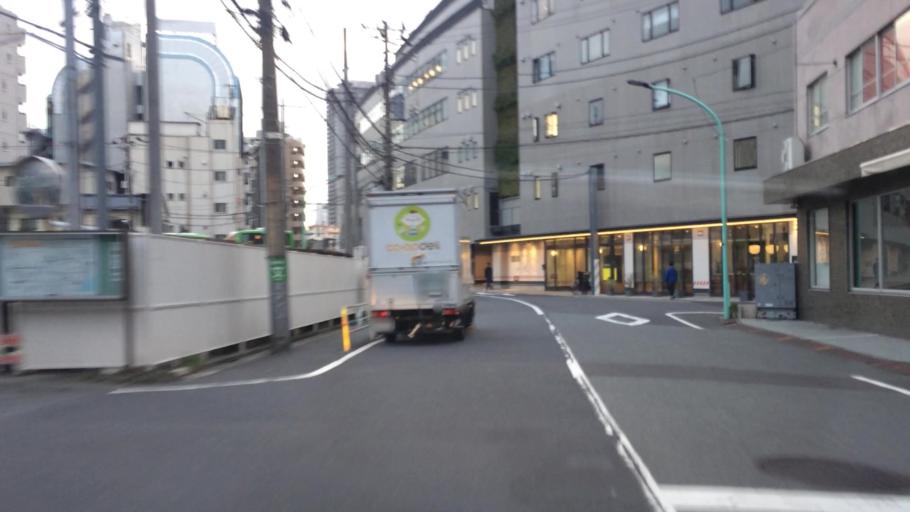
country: JP
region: Tokyo
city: Tokyo
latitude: 35.6534
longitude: 139.7075
